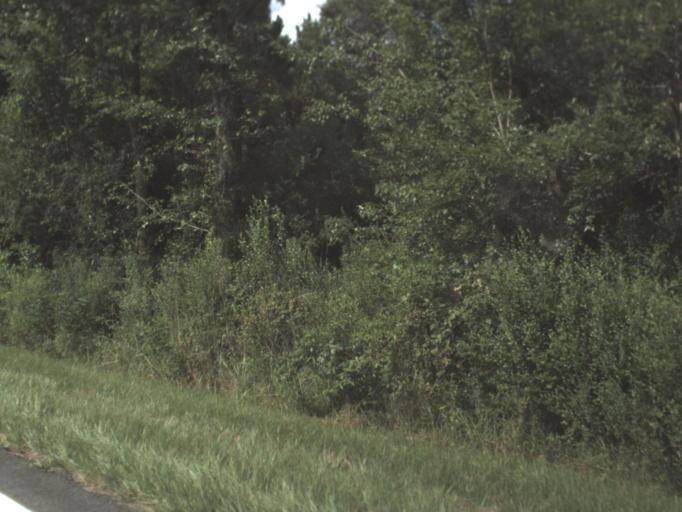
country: US
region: Florida
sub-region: Madison County
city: Madison
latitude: 30.3874
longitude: -83.6574
